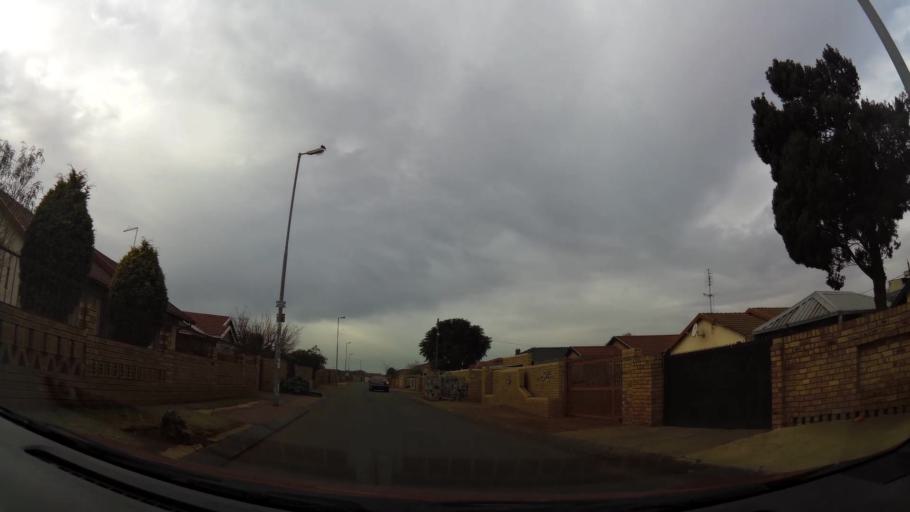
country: ZA
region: Gauteng
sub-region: City of Johannesburg Metropolitan Municipality
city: Soweto
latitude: -26.2795
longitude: 27.8424
